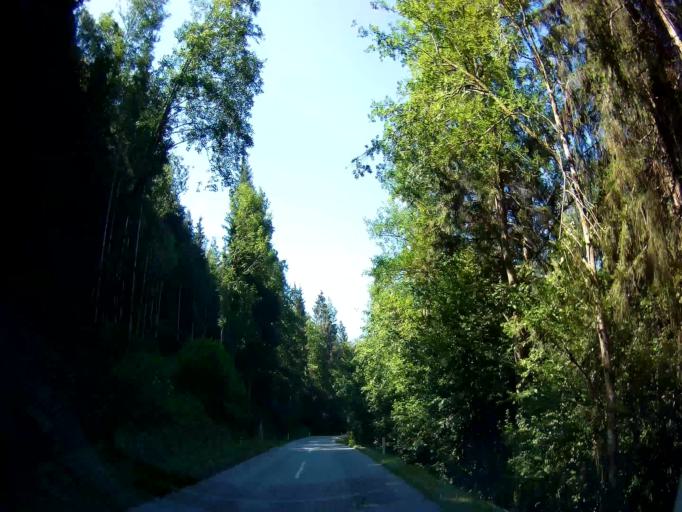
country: AT
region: Carinthia
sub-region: Politischer Bezirk Klagenfurt Land
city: Grafenstein
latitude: 46.6030
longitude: 14.4411
